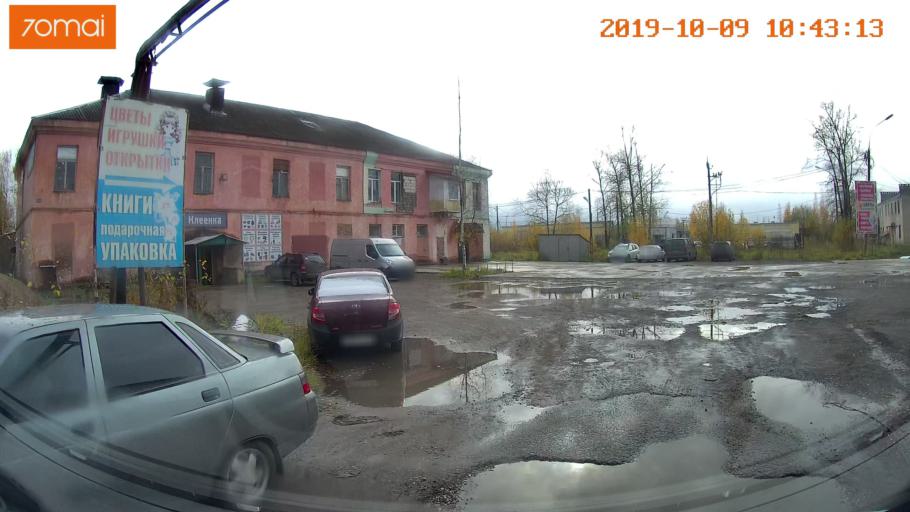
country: RU
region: Vologda
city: Vologda
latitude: 59.2371
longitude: 39.8155
